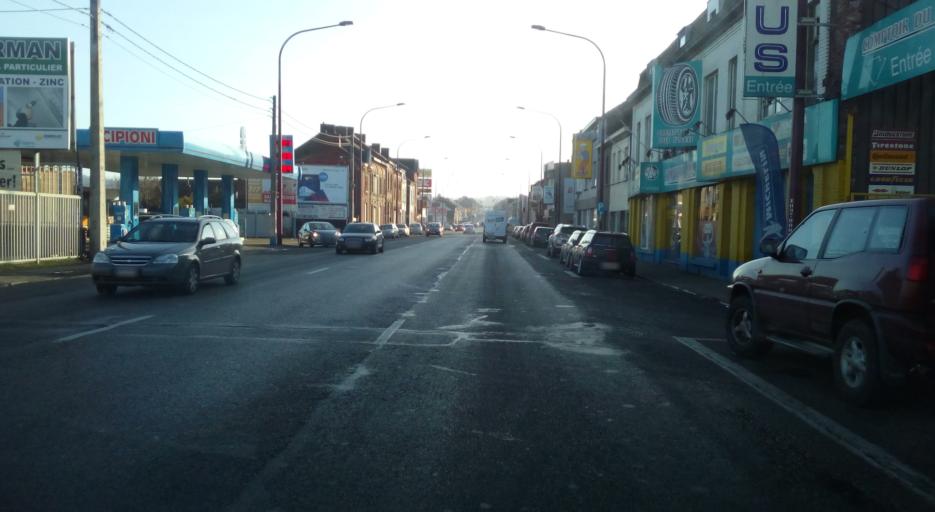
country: BE
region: Wallonia
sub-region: Province du Hainaut
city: Charleroi
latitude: 50.3972
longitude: 4.4548
